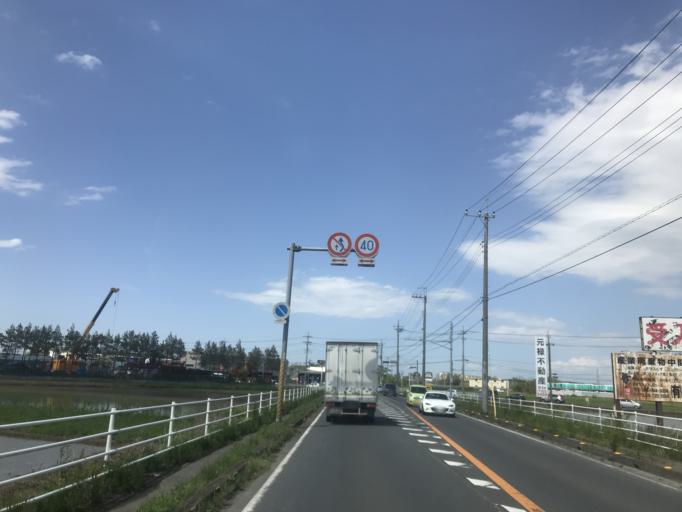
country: JP
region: Chiba
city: Noda
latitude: 35.9764
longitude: 139.8862
